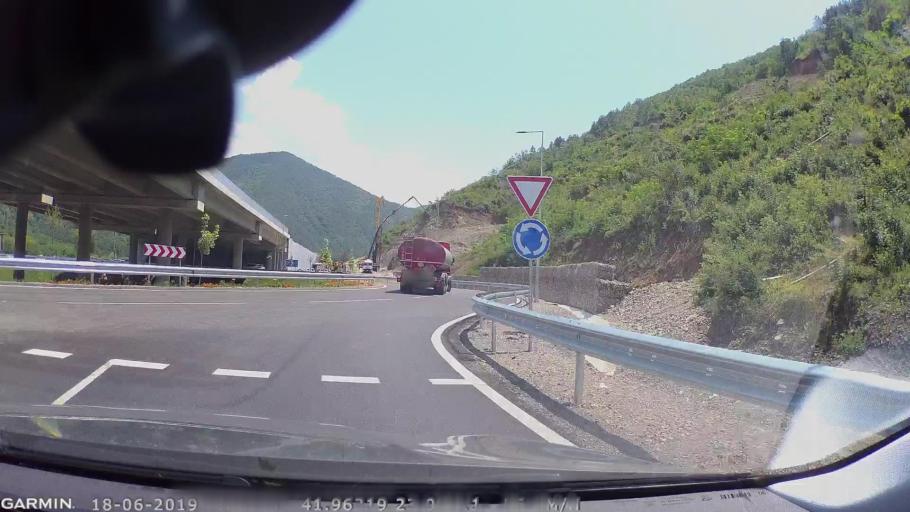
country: BG
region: Blagoevgrad
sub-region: Obshtina Blagoevgrad
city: Blagoevgrad
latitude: 41.9619
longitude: 23.0984
